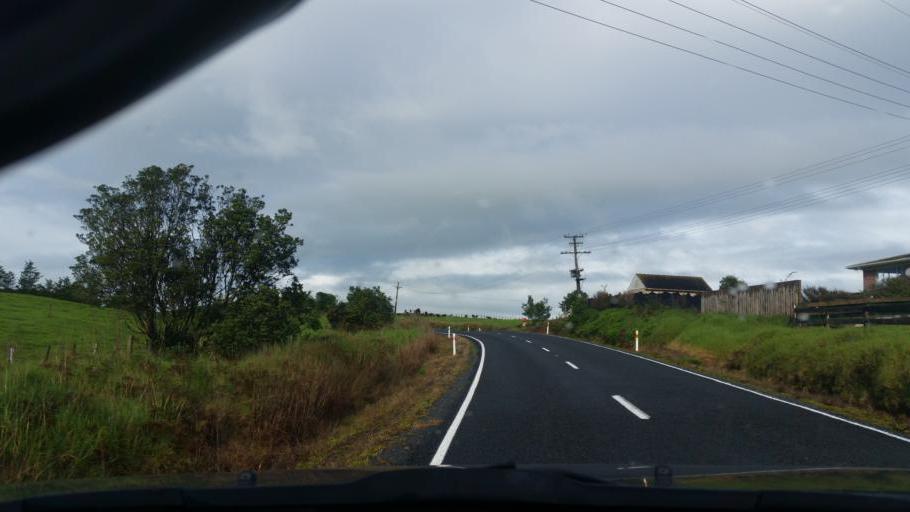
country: NZ
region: Northland
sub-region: Kaipara District
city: Dargaville
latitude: -35.9466
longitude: 173.7846
